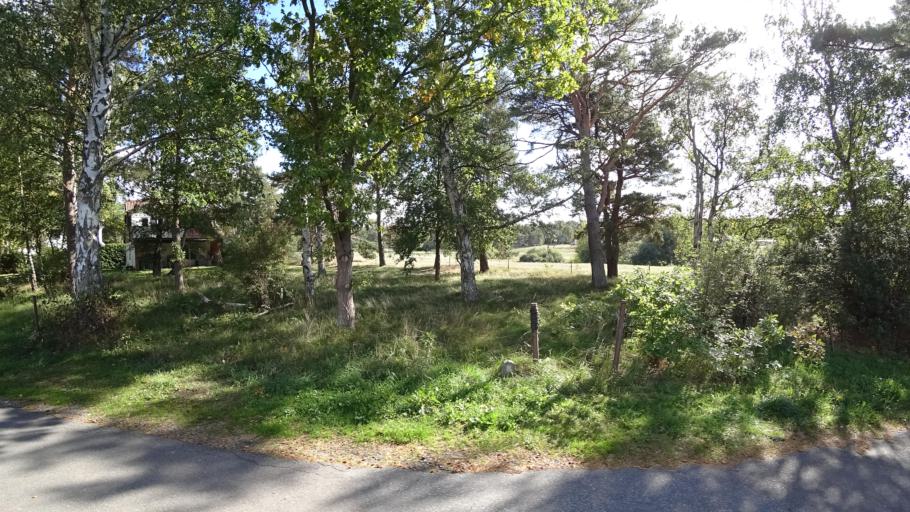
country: SE
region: Skane
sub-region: Kavlinge Kommun
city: Hofterup
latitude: 55.7586
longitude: 12.9751
